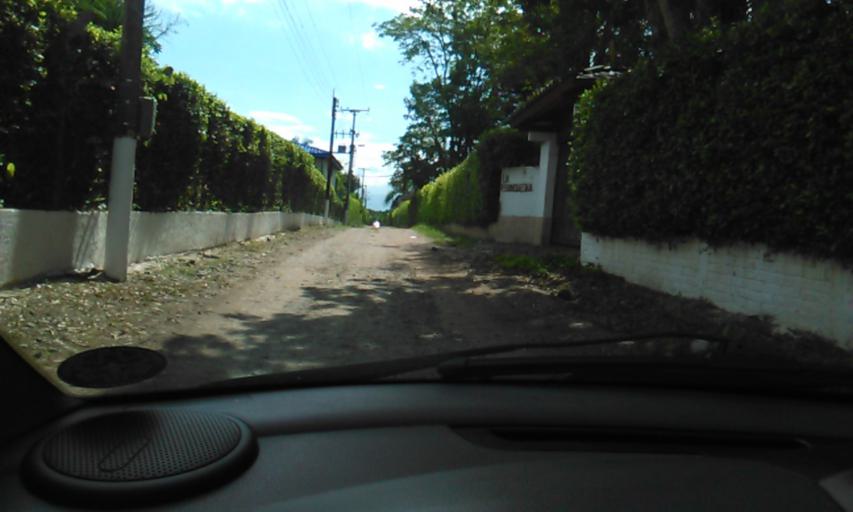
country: CO
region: Quindio
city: La Tebaida
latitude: 4.4427
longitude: -75.8465
